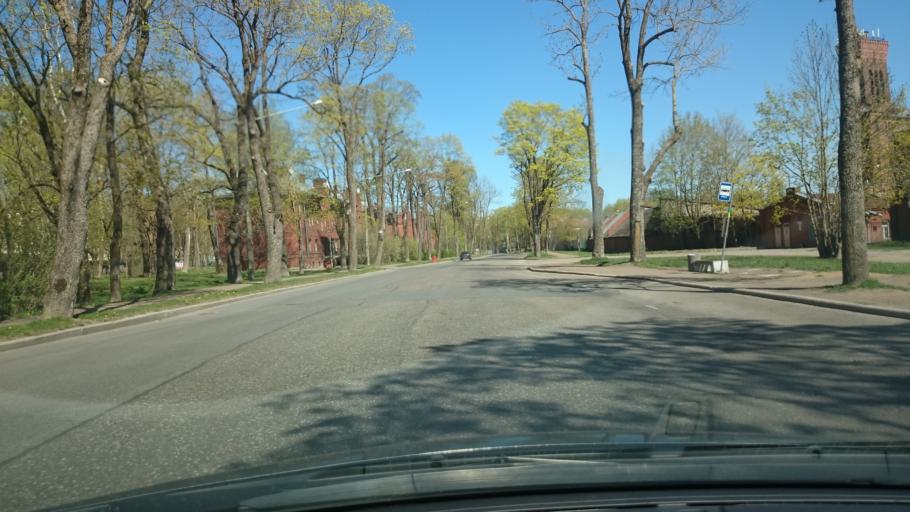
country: EE
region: Ida-Virumaa
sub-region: Narva linn
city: Narva
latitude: 59.3591
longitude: 28.1890
